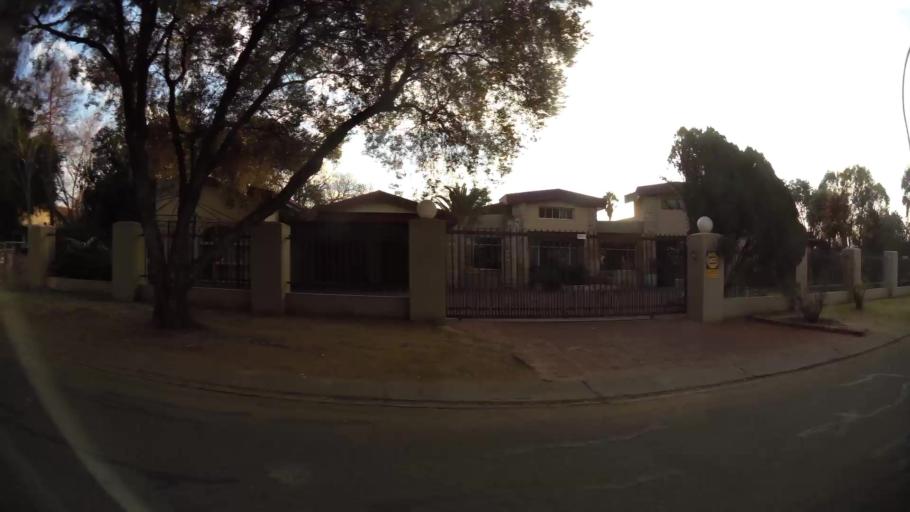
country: ZA
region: Orange Free State
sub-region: Mangaung Metropolitan Municipality
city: Bloemfontein
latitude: -29.1472
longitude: 26.1772
